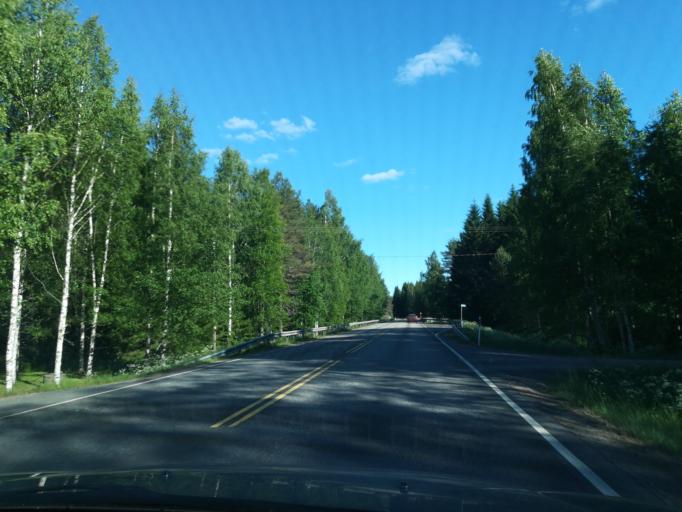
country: FI
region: South Karelia
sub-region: Imatra
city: Ruokolahti
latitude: 61.3687
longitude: 28.6779
